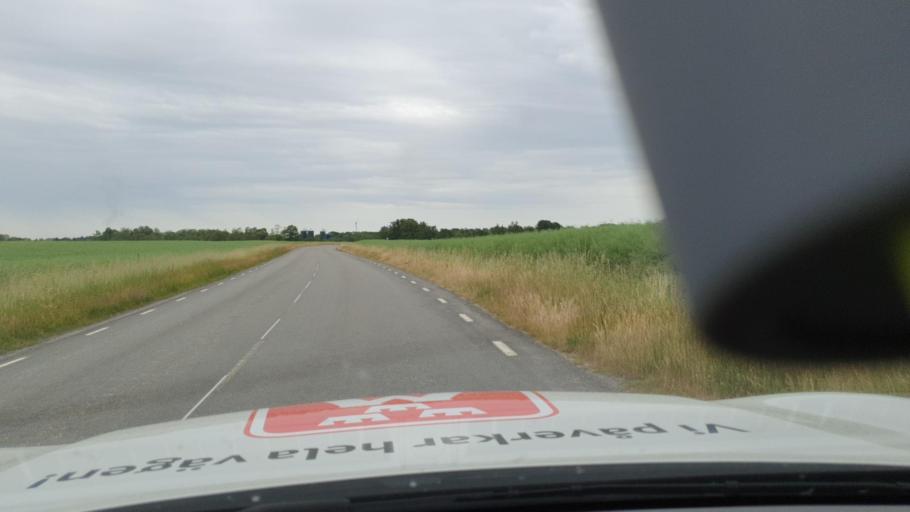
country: SE
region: Vaestra Goetaland
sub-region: Tidaholms Kommun
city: Olofstorp
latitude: 58.3017
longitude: 14.0819
